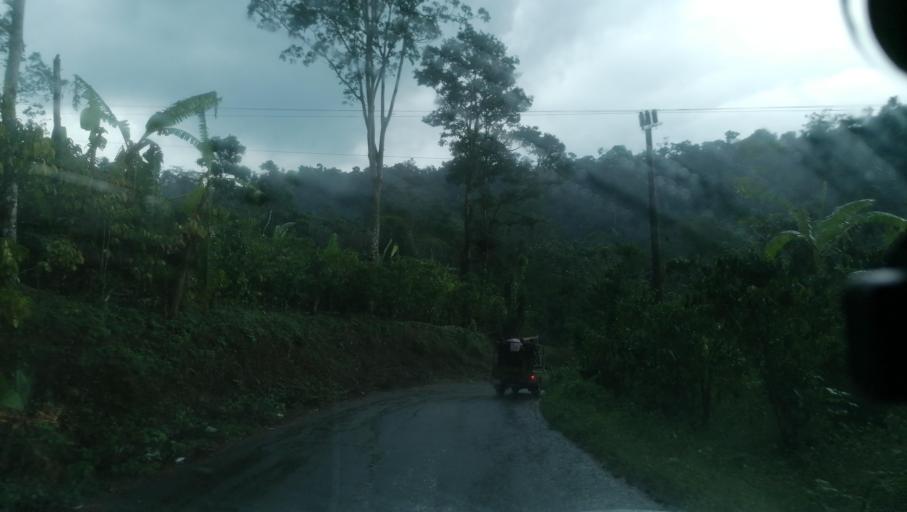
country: MX
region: Chiapas
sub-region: Cacahoatan
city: Benito Juarez
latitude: 15.0623
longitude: -92.1927
